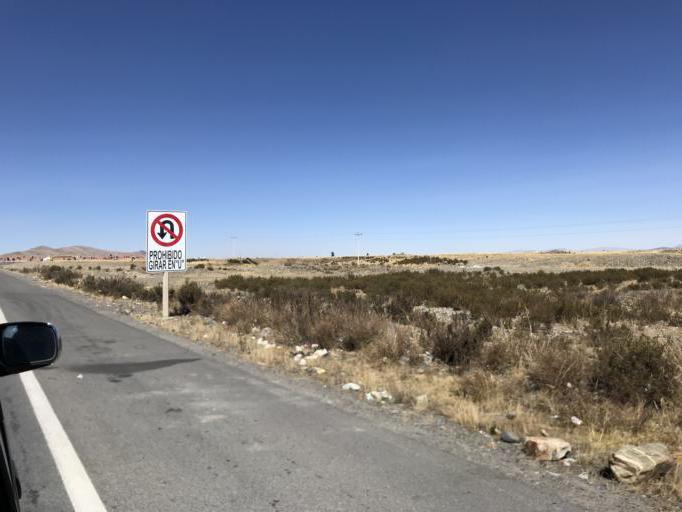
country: BO
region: La Paz
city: Batallas
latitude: -16.3227
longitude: -68.4320
